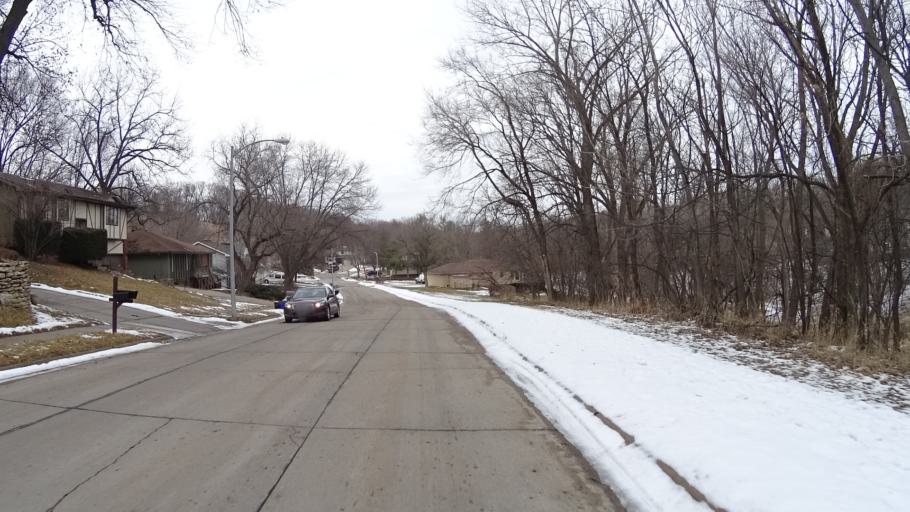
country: US
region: Nebraska
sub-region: Sarpy County
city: Bellevue
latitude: 41.1739
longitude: -95.9157
